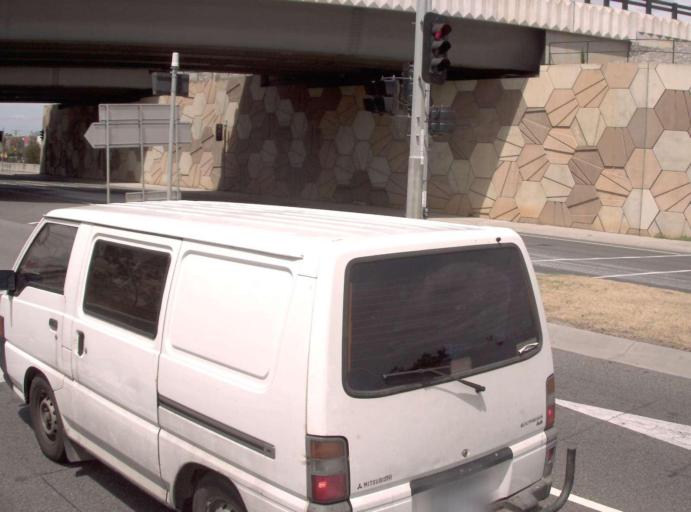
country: AU
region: Victoria
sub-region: Greater Dandenong
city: Dandenong
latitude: -37.9927
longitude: 145.1911
